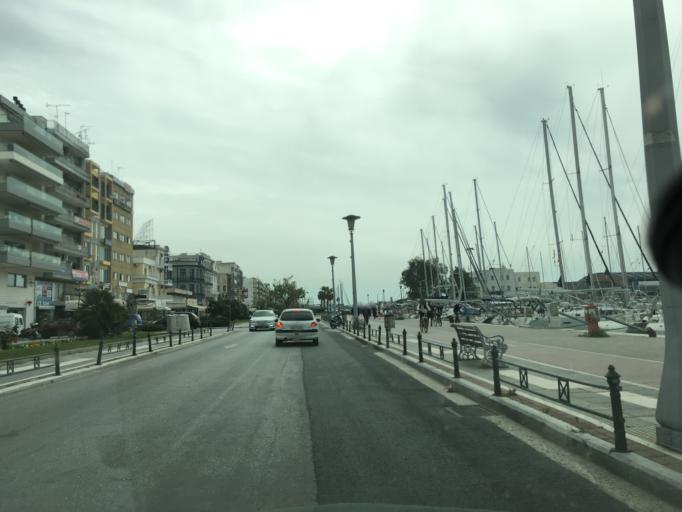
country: GR
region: Thessaly
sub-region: Nomos Magnisias
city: Volos
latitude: 39.3609
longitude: 22.9427
